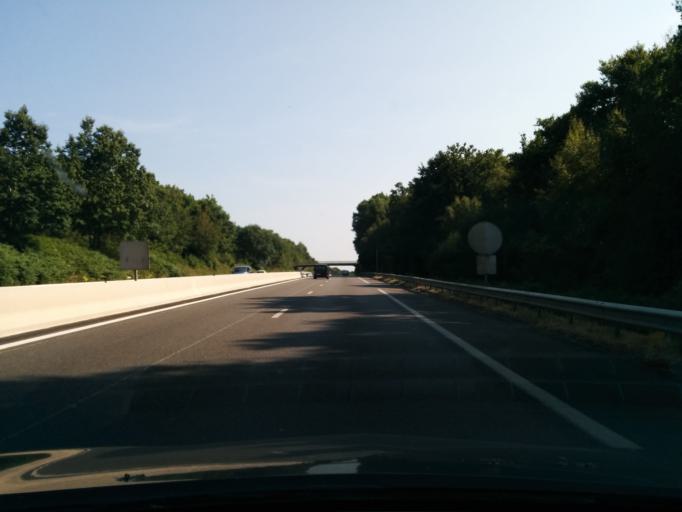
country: FR
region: Limousin
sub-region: Departement de la Haute-Vienne
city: Le Palais-sur-Vienne
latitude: 45.8689
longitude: 1.2876
